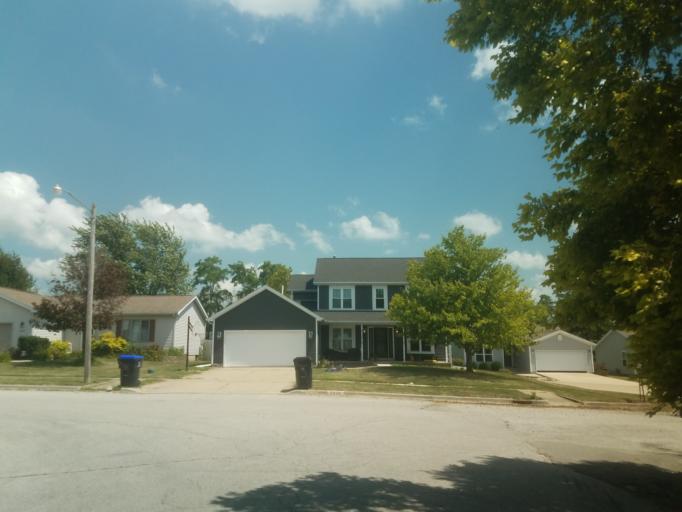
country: US
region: Illinois
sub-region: McLean County
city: Bloomington
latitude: 40.4414
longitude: -89.0315
